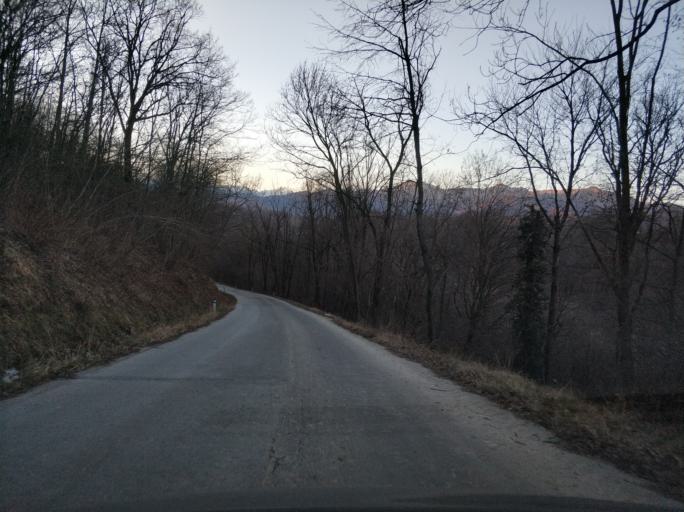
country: IT
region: Piedmont
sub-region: Provincia di Torino
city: Vauda Canavese Superiore
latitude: 45.2677
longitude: 7.6388
